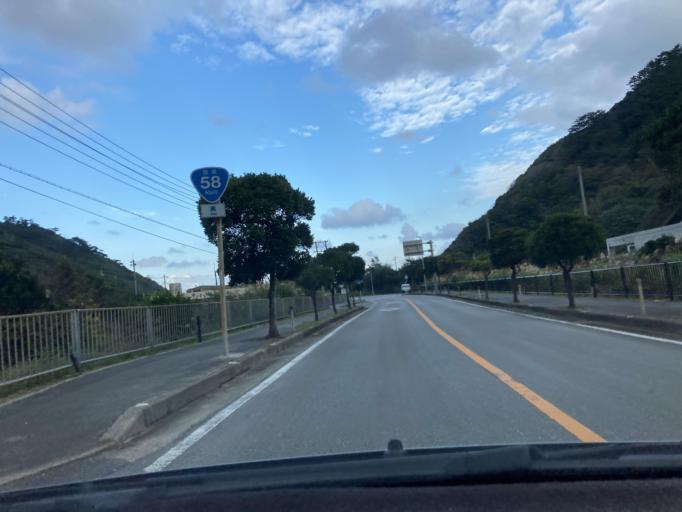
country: JP
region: Okinawa
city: Nago
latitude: 26.8368
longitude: 128.2871
